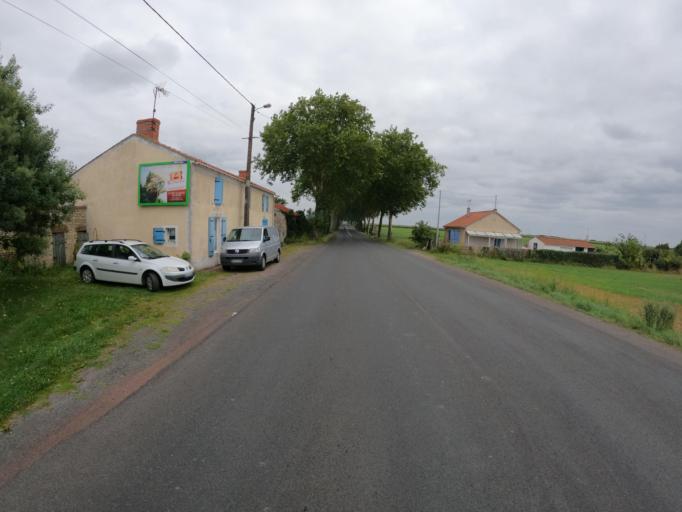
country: FR
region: Pays de la Loire
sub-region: Departement de la Vendee
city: Nalliers
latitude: 46.5249
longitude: -0.9947
